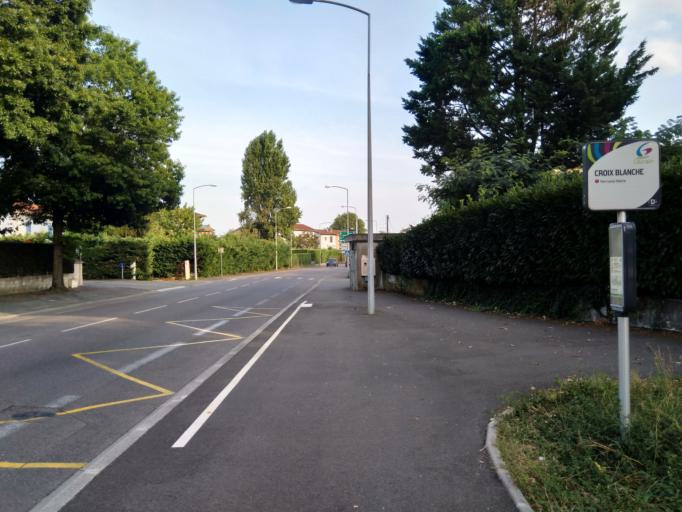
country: FR
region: Aquitaine
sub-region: Departement des Landes
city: Dax
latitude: 43.7079
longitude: -1.0392
